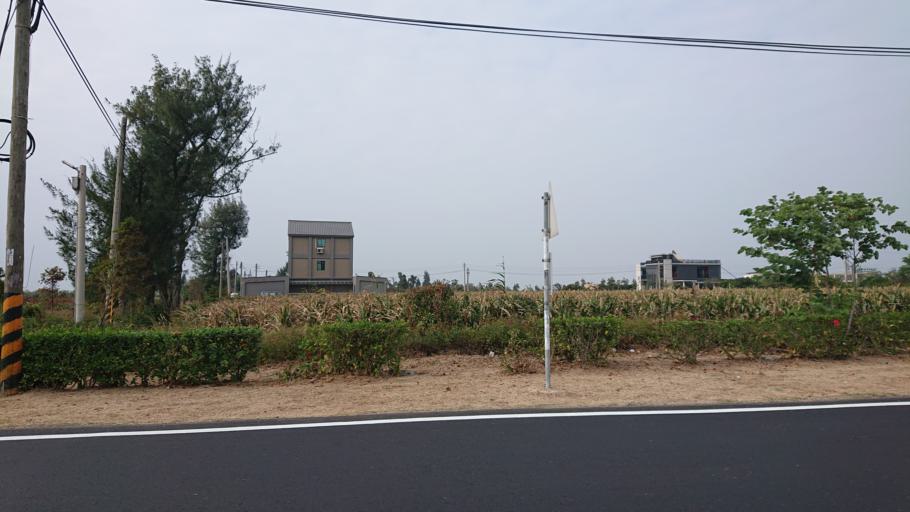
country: TW
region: Fukien
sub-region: Kinmen
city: Jincheng
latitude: 24.4595
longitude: 118.3814
